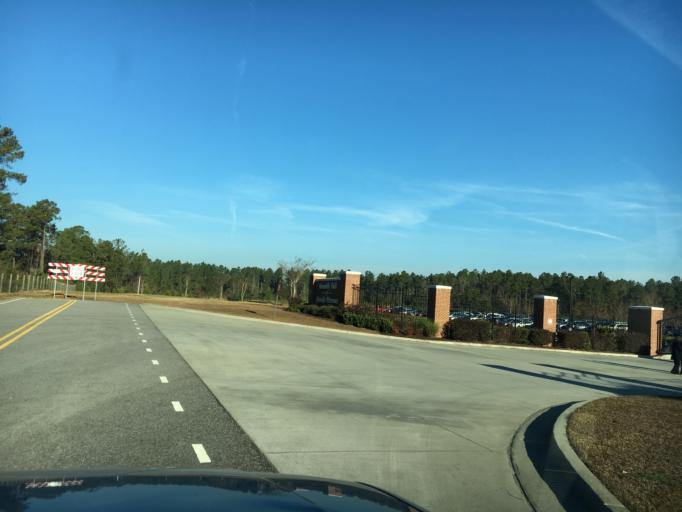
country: US
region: South Carolina
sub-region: Orangeburg County
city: Brookdale
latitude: 33.5240
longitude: -80.7945
